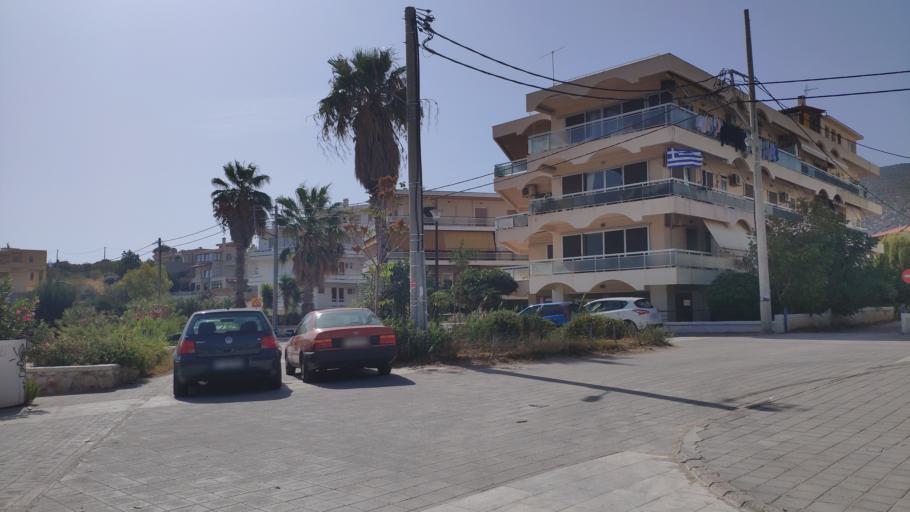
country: GR
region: Attica
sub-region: Nomarchia Anatolikis Attikis
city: Limin Mesoyaias
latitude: 37.8882
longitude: 24.0084
